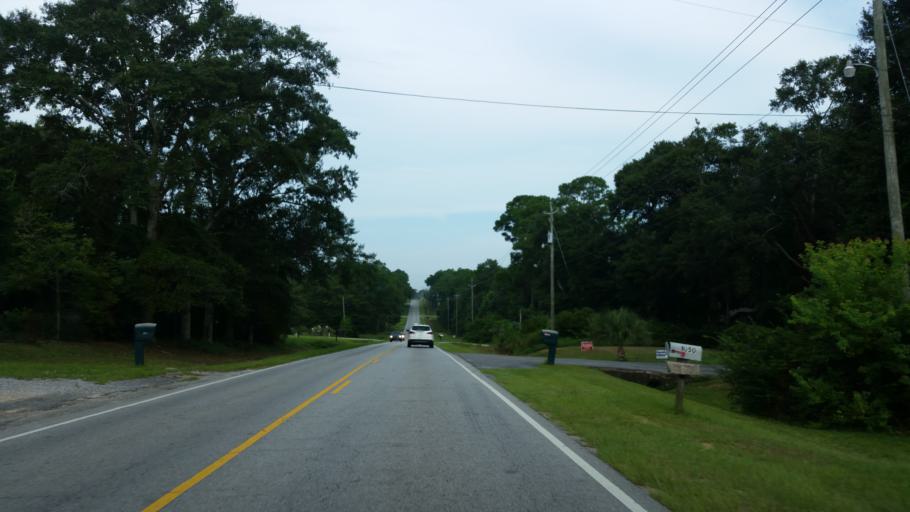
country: US
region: Florida
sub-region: Escambia County
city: Gonzalez
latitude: 30.5631
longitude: -87.3010
